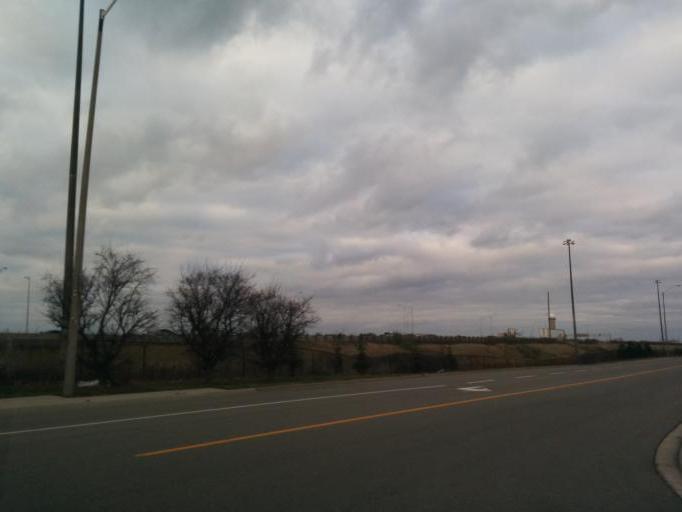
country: CA
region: Ontario
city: Etobicoke
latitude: 43.6615
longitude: -79.6078
